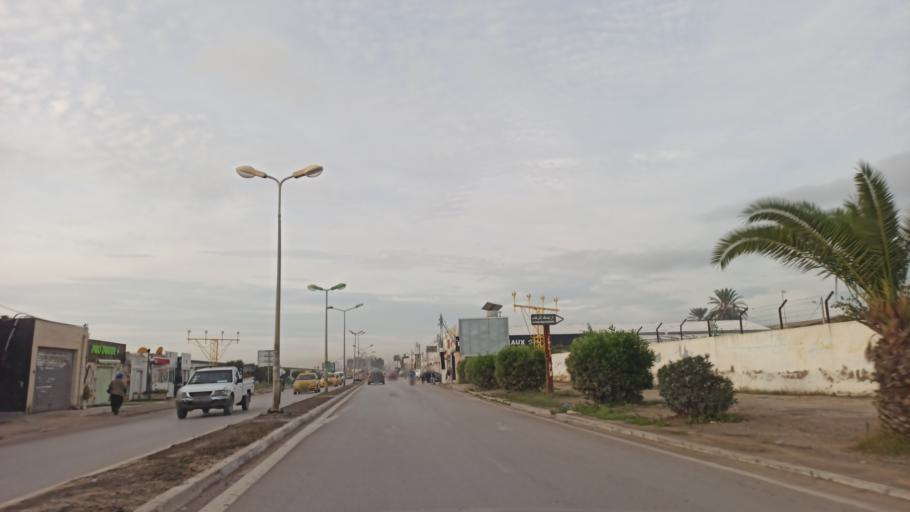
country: TN
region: Ariana
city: Ariana
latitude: 36.8717
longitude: 10.2330
